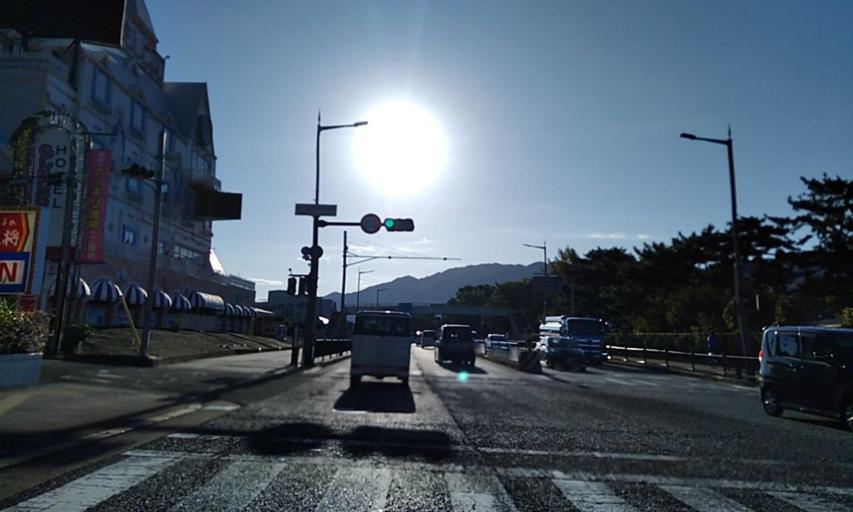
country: JP
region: Wakayama
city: Kainan
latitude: 34.1601
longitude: 135.1930
